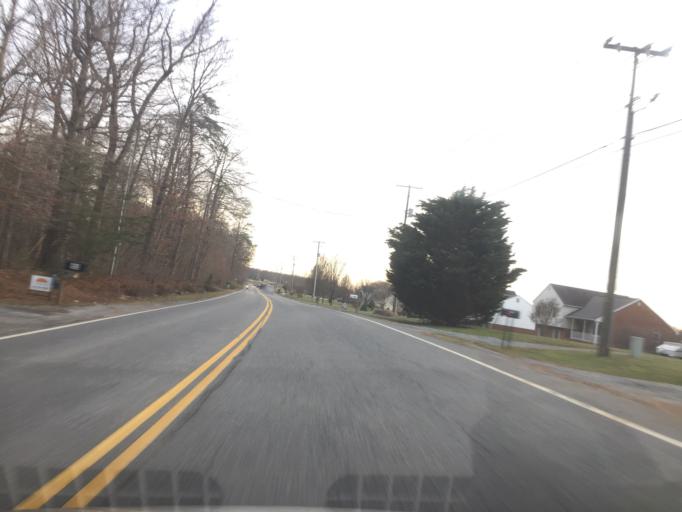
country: US
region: Virginia
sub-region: Bedford County
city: Forest
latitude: 37.3410
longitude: -79.2850
